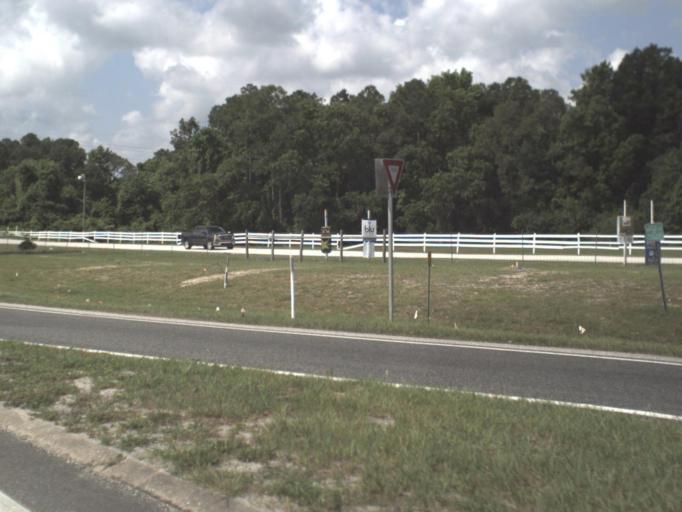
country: US
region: Florida
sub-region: Flagler County
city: Palm Coast
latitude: 29.6612
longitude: -81.2876
